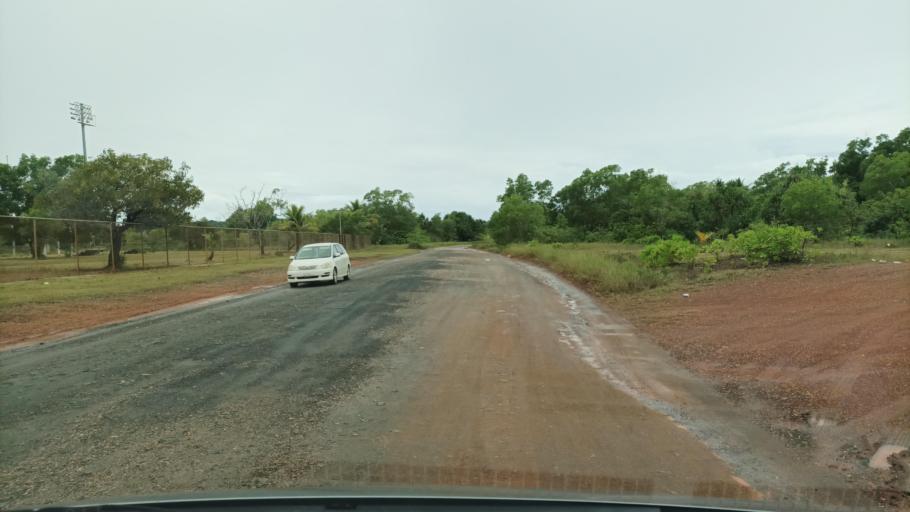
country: FM
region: Yap
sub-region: Weloy Municipality
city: Colonia
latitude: 9.5459
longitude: 138.1650
